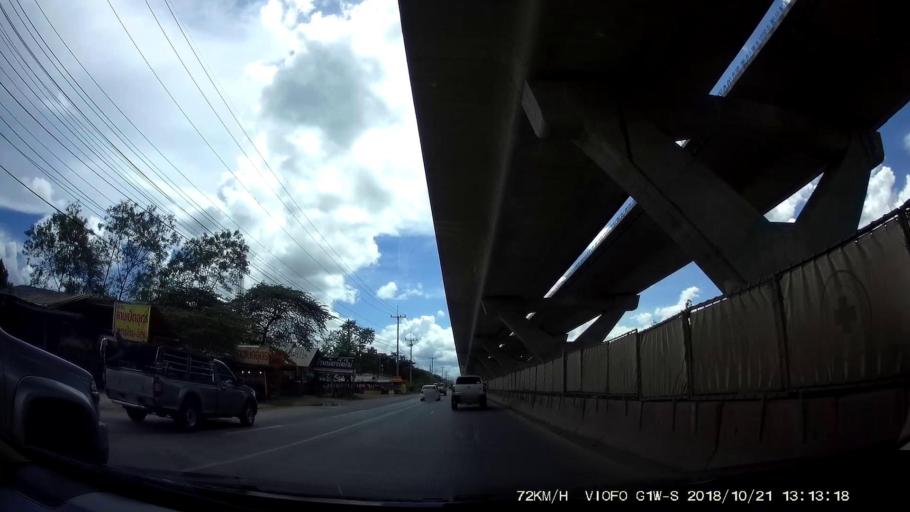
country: TH
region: Nakhon Ratchasima
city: Pak Chong
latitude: 14.7808
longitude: 101.5236
